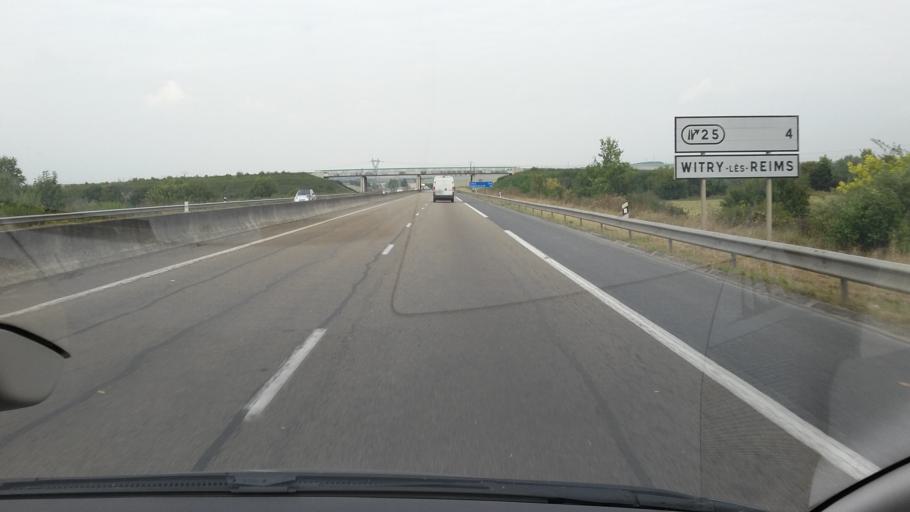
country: FR
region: Champagne-Ardenne
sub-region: Departement de la Marne
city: Cernay-les-Reims
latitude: 49.2489
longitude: 4.0827
